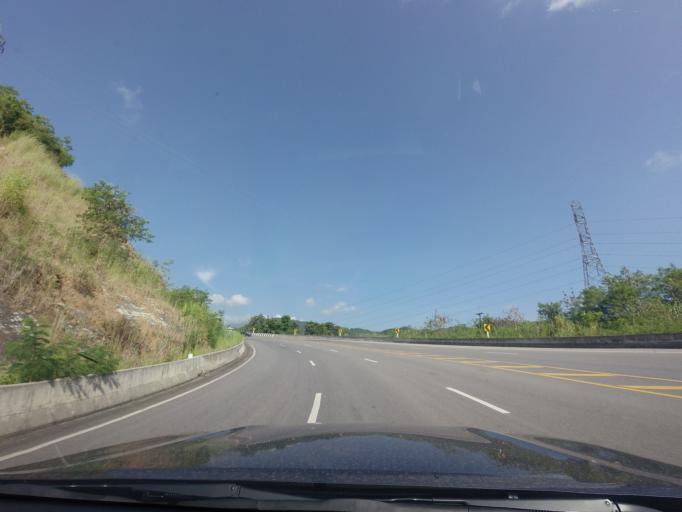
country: TH
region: Phetchabun
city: Lom Sak
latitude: 16.7784
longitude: 101.1180
